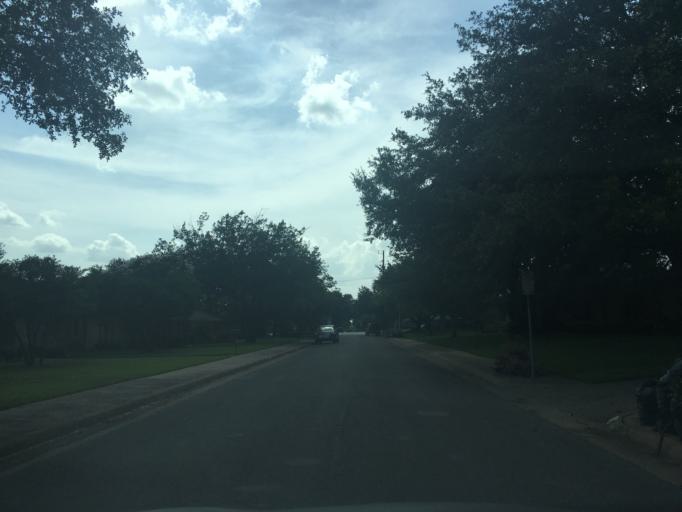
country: US
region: Texas
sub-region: Dallas County
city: Addison
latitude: 32.9164
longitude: -96.8364
